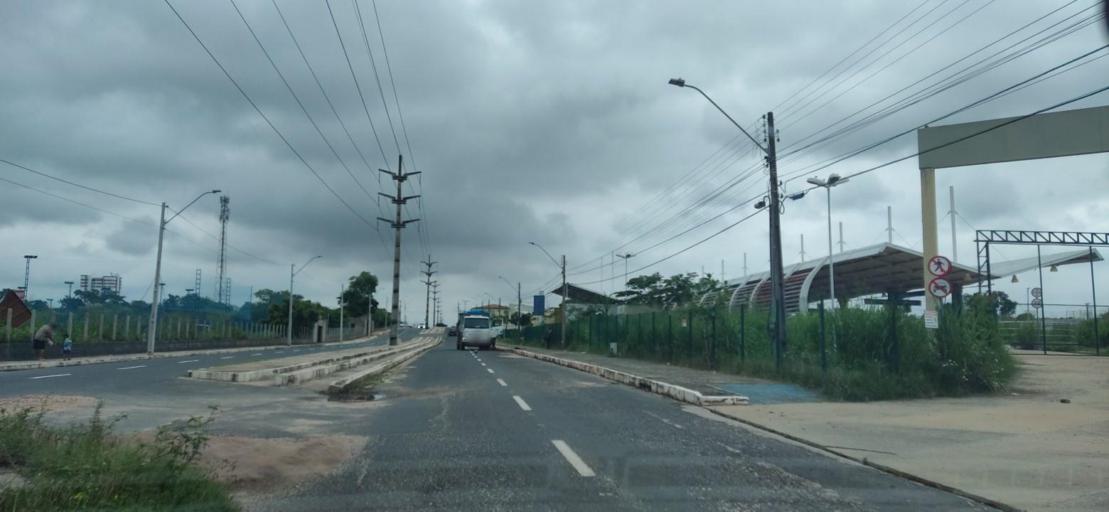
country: BR
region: Piaui
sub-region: Teresina
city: Teresina
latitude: -5.0628
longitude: -42.7515
